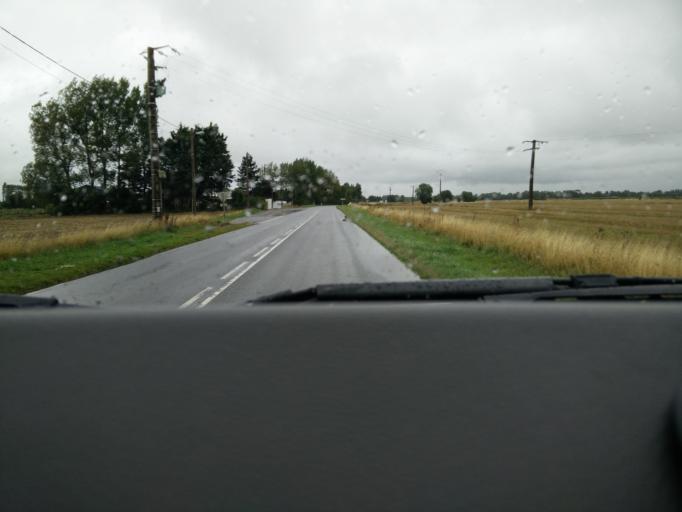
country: FR
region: Picardie
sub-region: Departement de la Somme
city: Le Crotoy
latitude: 50.2266
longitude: 1.6387
